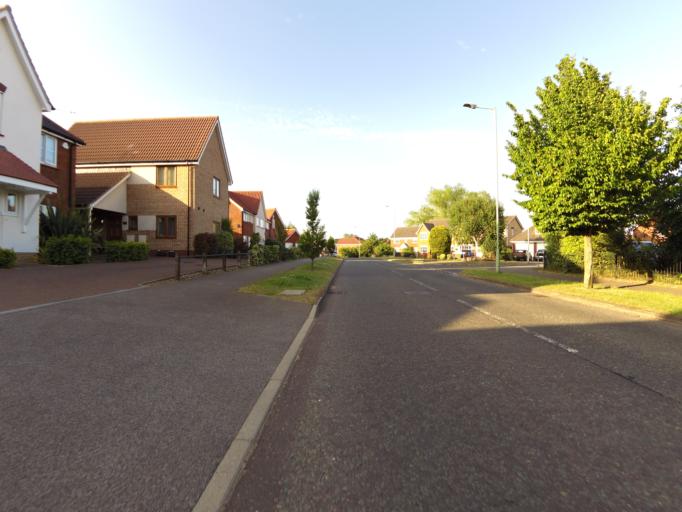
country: GB
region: England
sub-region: Suffolk
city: Kesgrave
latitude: 52.0536
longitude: 1.2184
